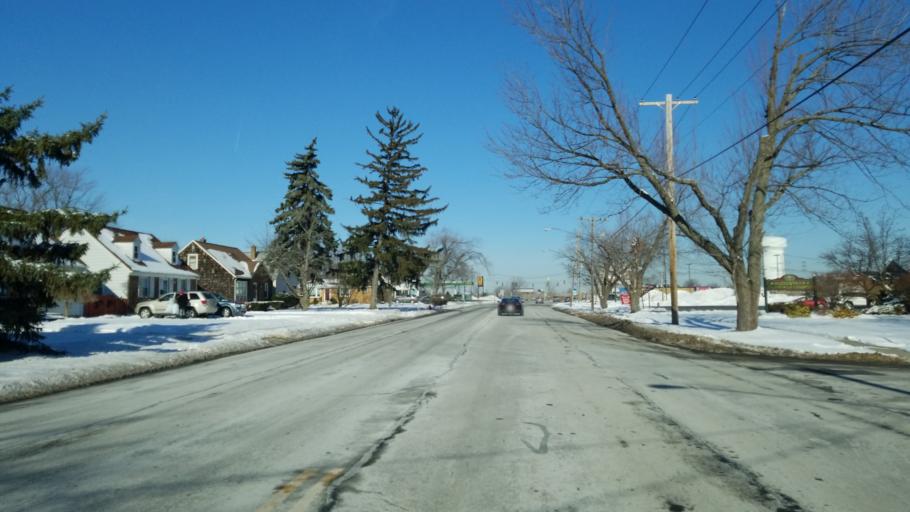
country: US
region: New York
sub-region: Erie County
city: Tonawanda
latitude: 42.9967
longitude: -78.8497
